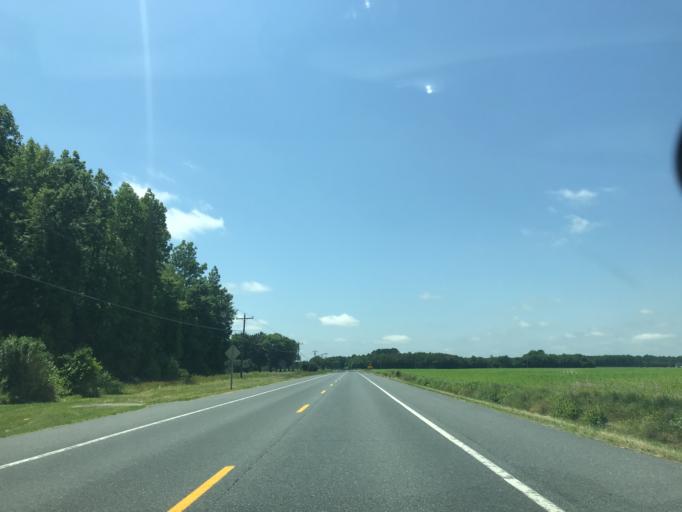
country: US
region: Maryland
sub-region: Caroline County
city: Federalsburg
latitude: 38.6312
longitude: -75.7399
